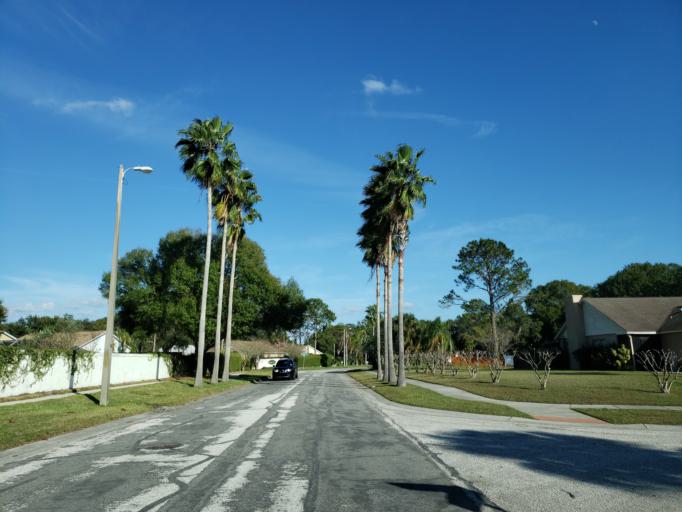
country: US
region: Florida
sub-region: Hillsborough County
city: Balm
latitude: 27.7905
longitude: -82.3203
